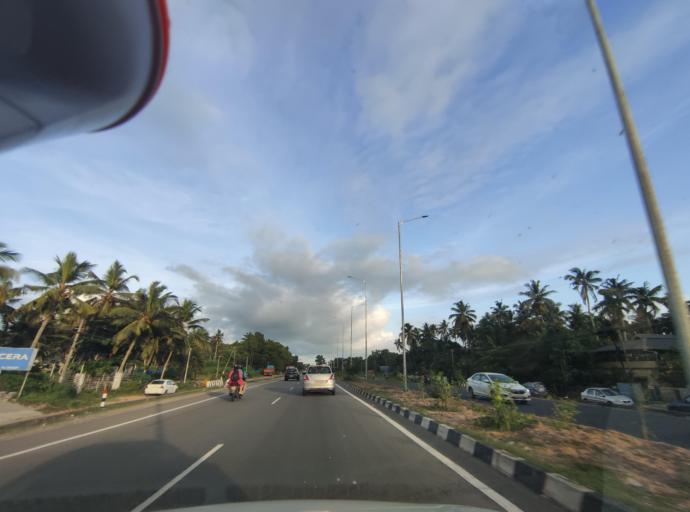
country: IN
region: Kerala
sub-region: Thiruvananthapuram
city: Thiruvananthapuram
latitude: 8.5057
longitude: 76.9110
